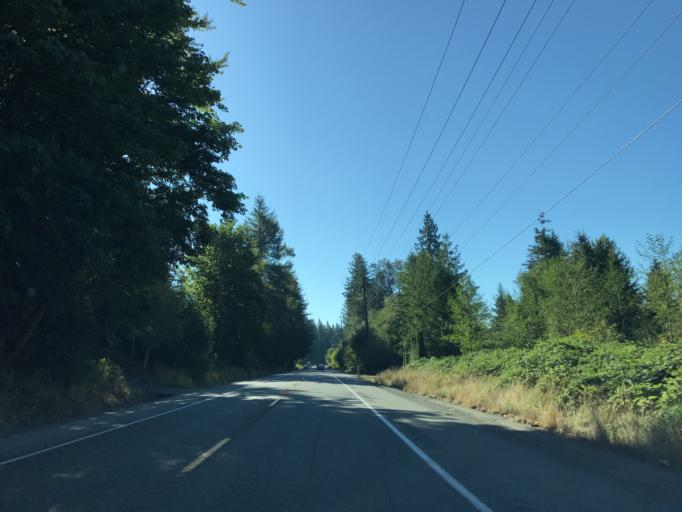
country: US
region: Washington
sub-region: King County
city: Black Diamond
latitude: 47.2916
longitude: -121.9950
